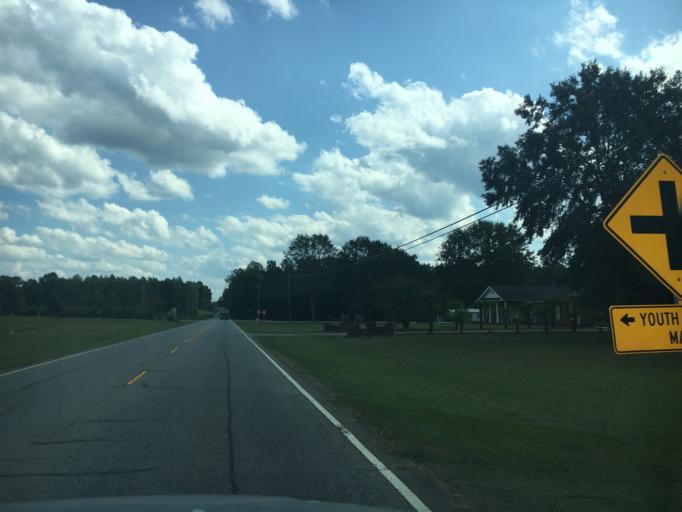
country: US
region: South Carolina
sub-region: Anderson County
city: Williamston
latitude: 34.5730
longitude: -82.4936
